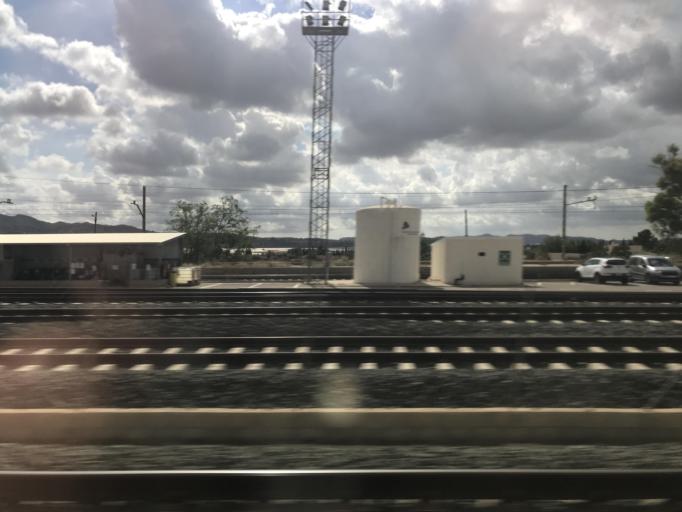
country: ES
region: Valencia
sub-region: Provincia de Alicante
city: Monforte del Cid
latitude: 38.4077
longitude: -0.6935
